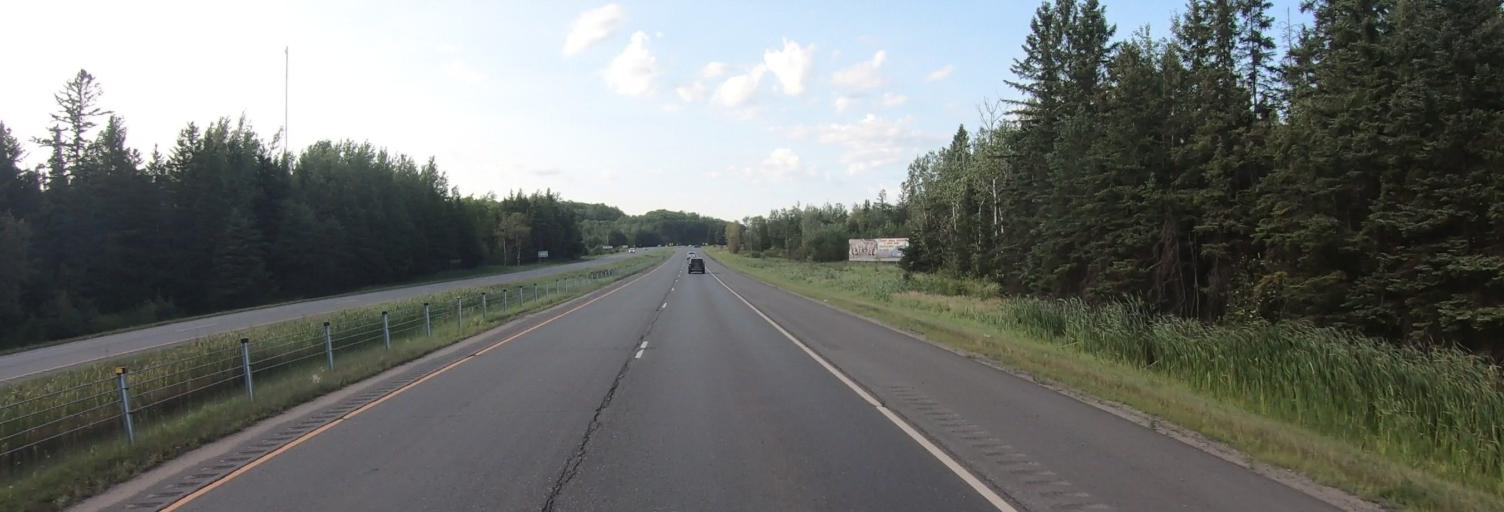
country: US
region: Minnesota
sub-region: Saint Louis County
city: Eveleth
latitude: 47.4804
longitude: -92.5303
